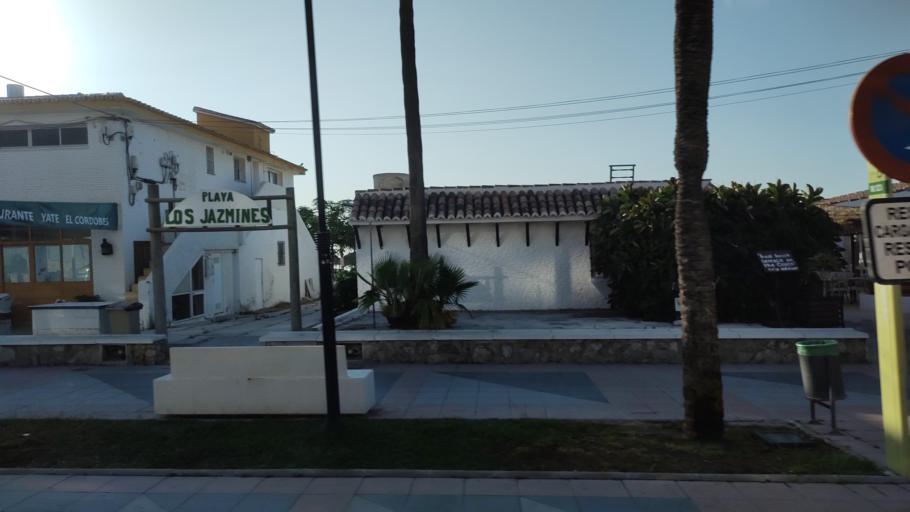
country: ES
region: Andalusia
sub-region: Provincia de Malaga
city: Torremolinos
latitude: 36.6273
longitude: -4.4917
